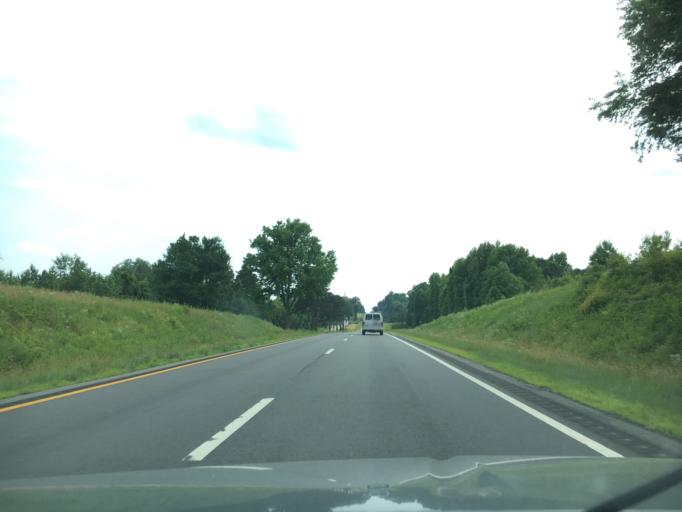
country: US
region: Virginia
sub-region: Mecklenburg County
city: Chase City
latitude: 36.9180
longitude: -78.5202
